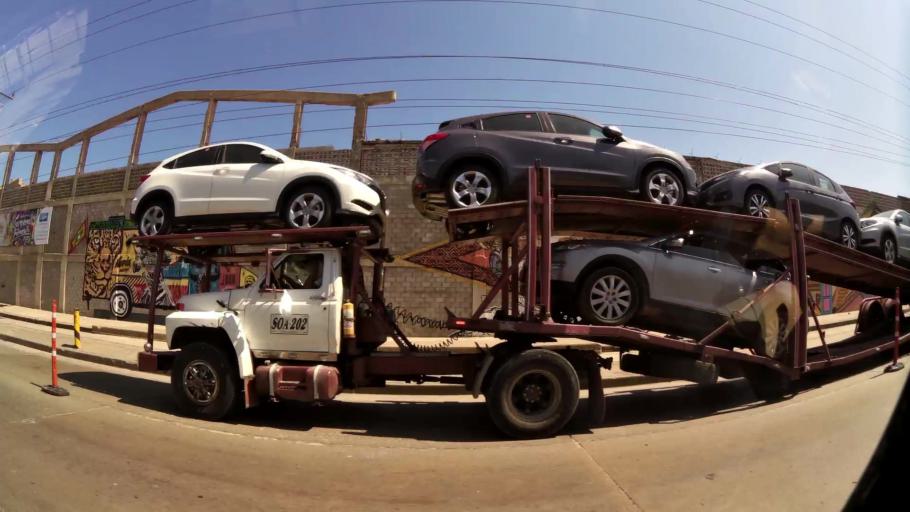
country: CO
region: Atlantico
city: Barranquilla
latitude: 11.0171
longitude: -74.7960
